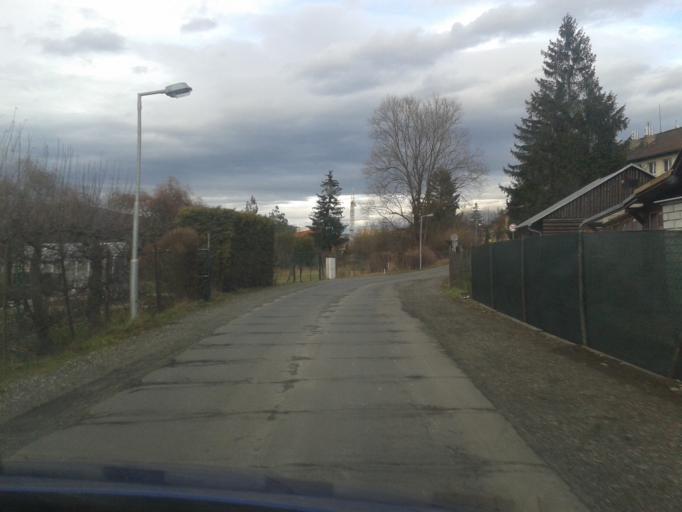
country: CZ
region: Central Bohemia
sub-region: Okres Beroun
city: Kraluv Dvur
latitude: 49.9351
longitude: 14.0281
